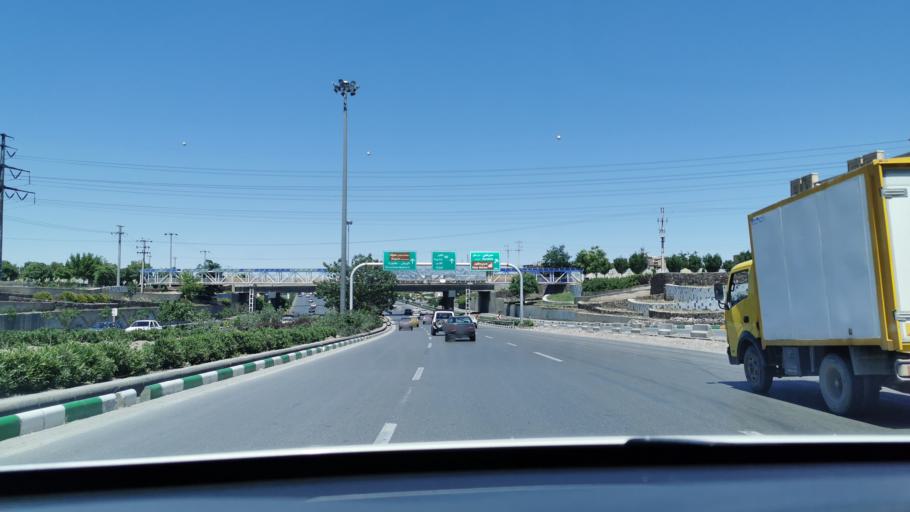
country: IR
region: Razavi Khorasan
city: Mashhad
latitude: 36.2620
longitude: 59.6502
